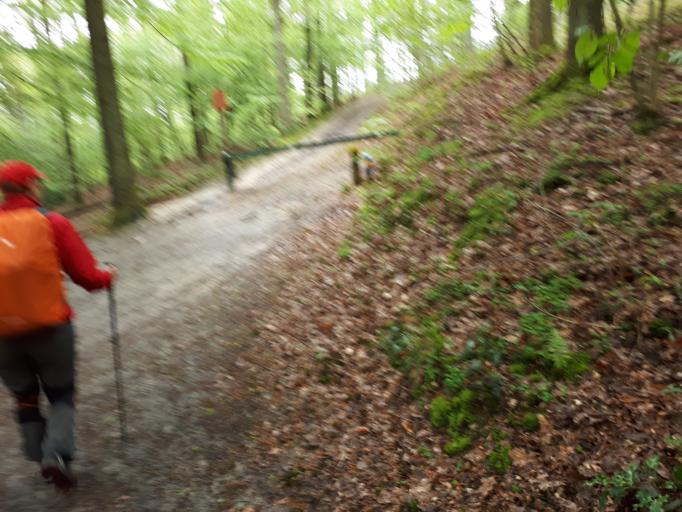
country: BE
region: Wallonia
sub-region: Province de Liege
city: Plombieres
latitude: 50.7725
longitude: 5.9576
